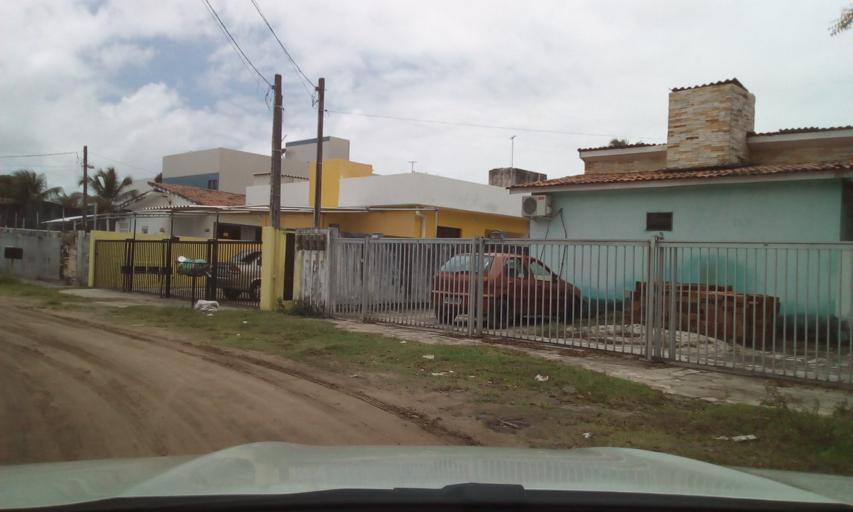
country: BR
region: Paraiba
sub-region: Conde
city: Conde
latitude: -7.2153
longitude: -34.8402
